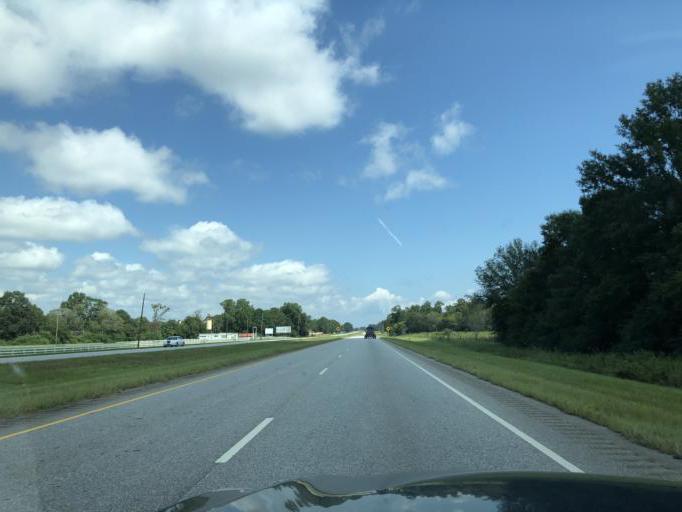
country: US
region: Alabama
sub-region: Barbour County
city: Eufaula
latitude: 31.7899
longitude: -85.1710
